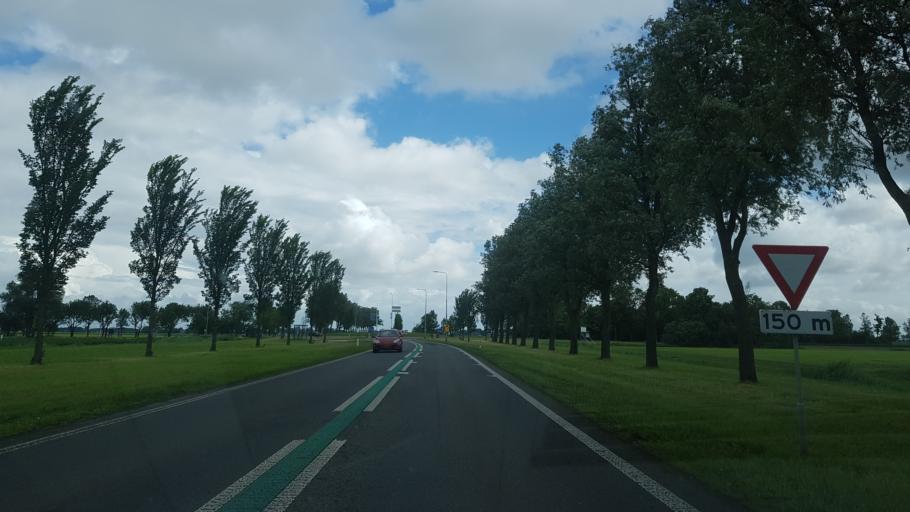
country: NL
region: Friesland
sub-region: Gemeente Dongeradeel
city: Anjum
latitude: 53.3566
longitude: 6.0734
